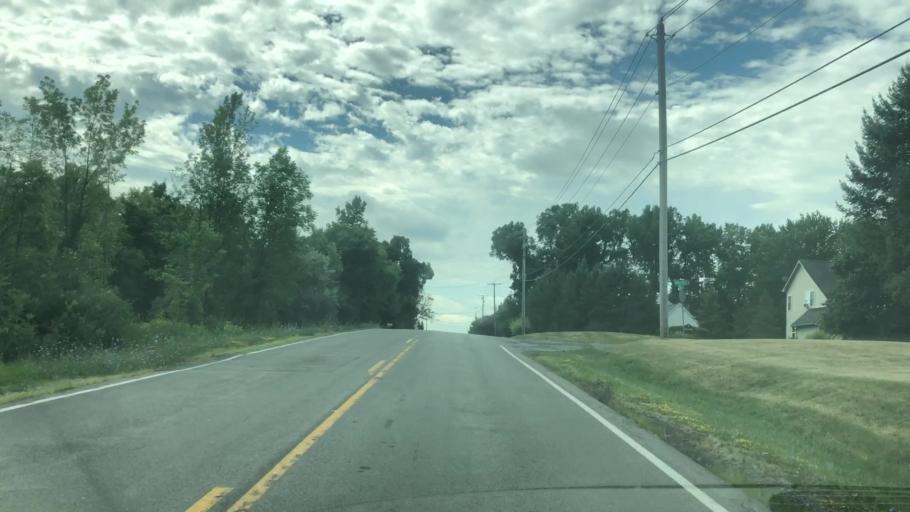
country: US
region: New York
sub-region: Monroe County
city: Fairport
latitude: 43.0700
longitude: -77.3921
